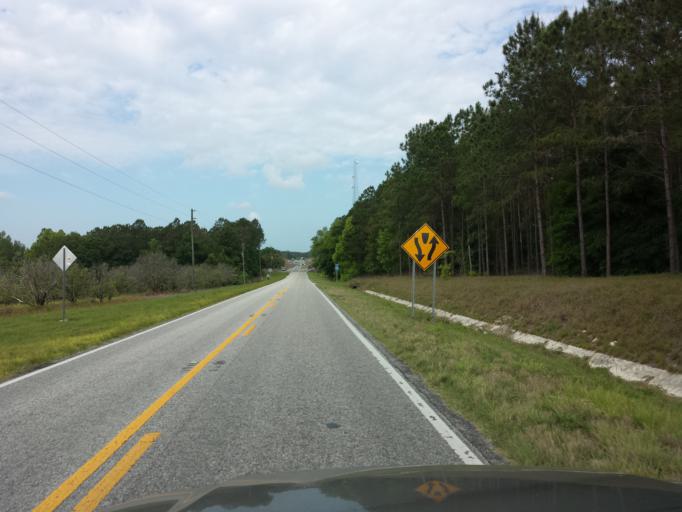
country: US
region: Florida
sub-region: Pasco County
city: San Antonio
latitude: 28.4199
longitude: -82.2826
